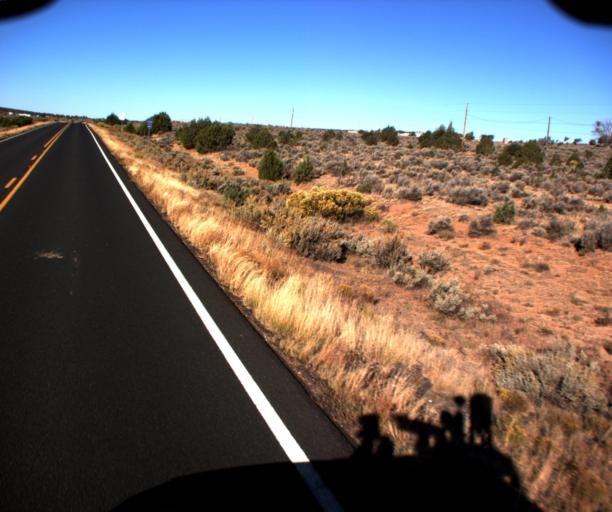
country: US
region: Arizona
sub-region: Apache County
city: Ganado
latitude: 35.7606
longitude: -109.7619
